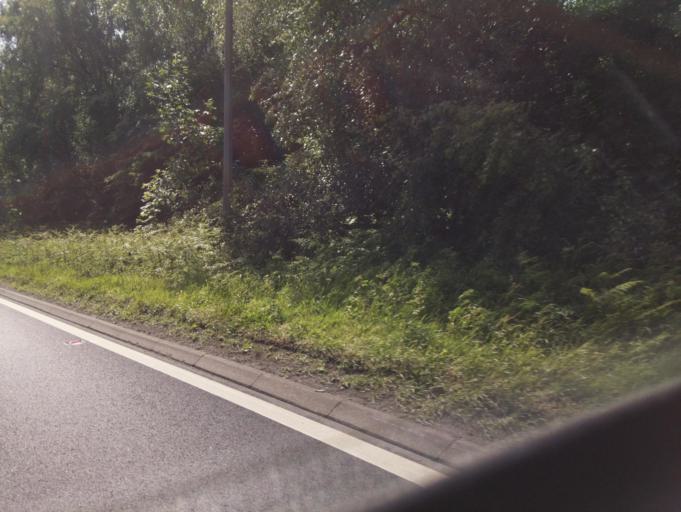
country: GB
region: England
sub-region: North Lincolnshire
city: Manton
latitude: 53.5581
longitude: -0.5921
